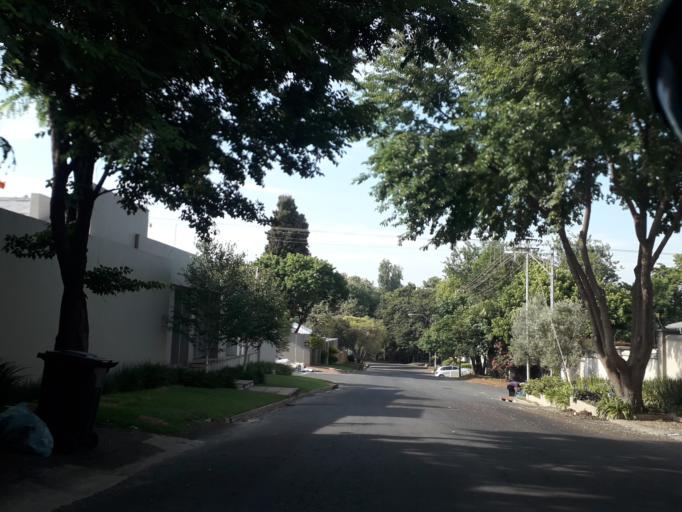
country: ZA
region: Gauteng
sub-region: City of Johannesburg Metropolitan Municipality
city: Johannesburg
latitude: -26.1388
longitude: 28.0156
